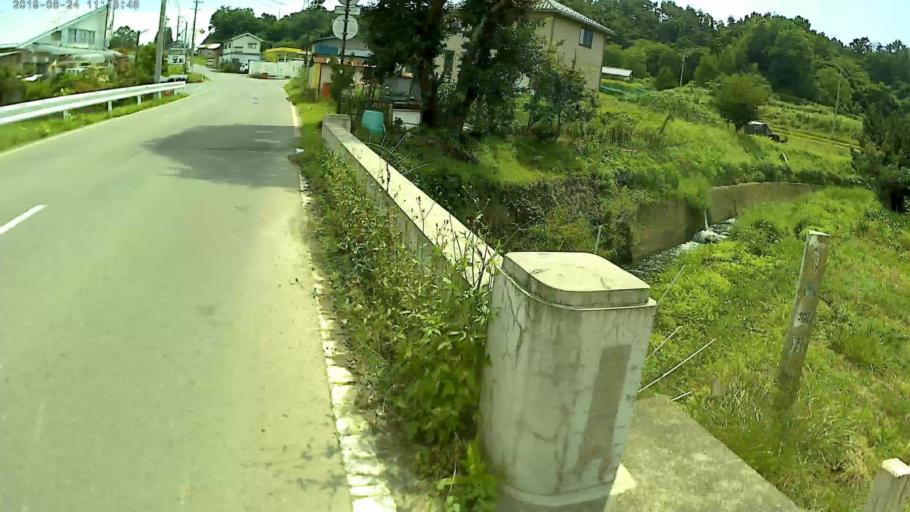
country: JP
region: Nagano
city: Kamimaruko
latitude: 36.2716
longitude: 138.3224
